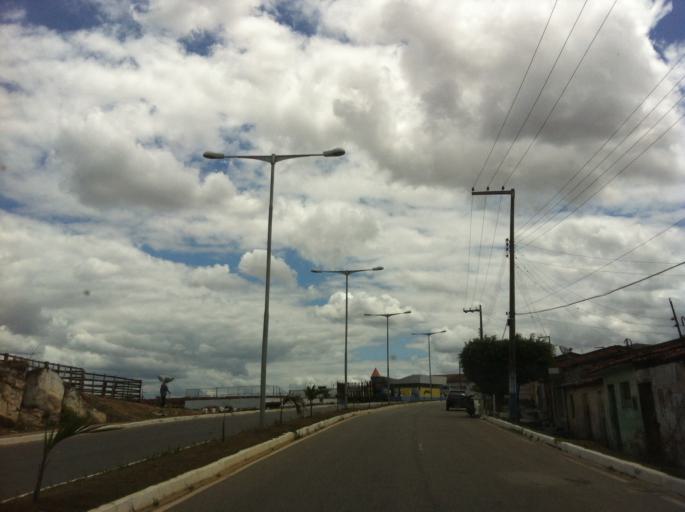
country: BR
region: Alagoas
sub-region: Ibateguara
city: Ibateguara
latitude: -8.9657
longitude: -35.9212
